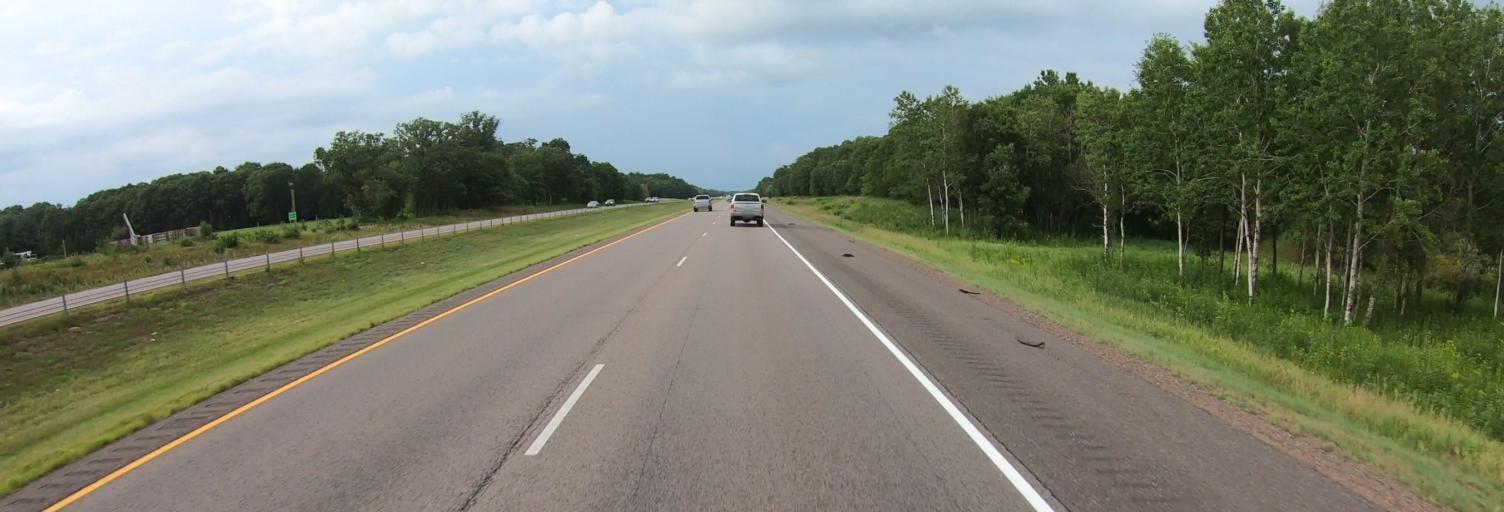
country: US
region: Minnesota
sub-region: Chisago County
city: Wyoming
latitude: 45.3602
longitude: -92.9967
